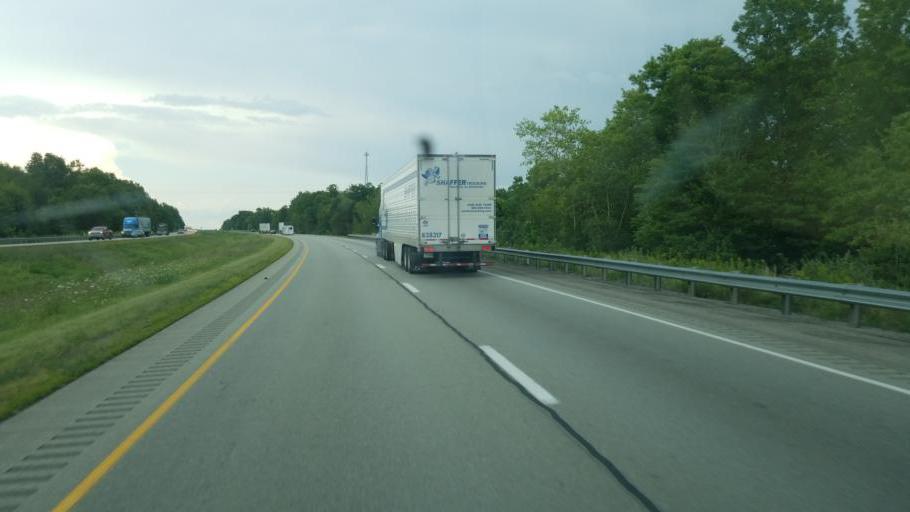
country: US
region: Pennsylvania
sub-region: Mercer County
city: Grove City
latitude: 41.1957
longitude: -80.1058
